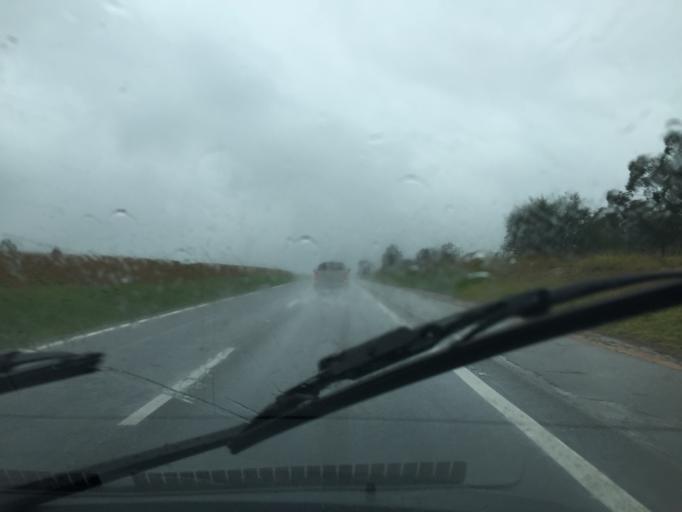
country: BR
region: Sao Paulo
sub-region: Itu
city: Itu
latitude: -23.3925
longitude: -47.3322
